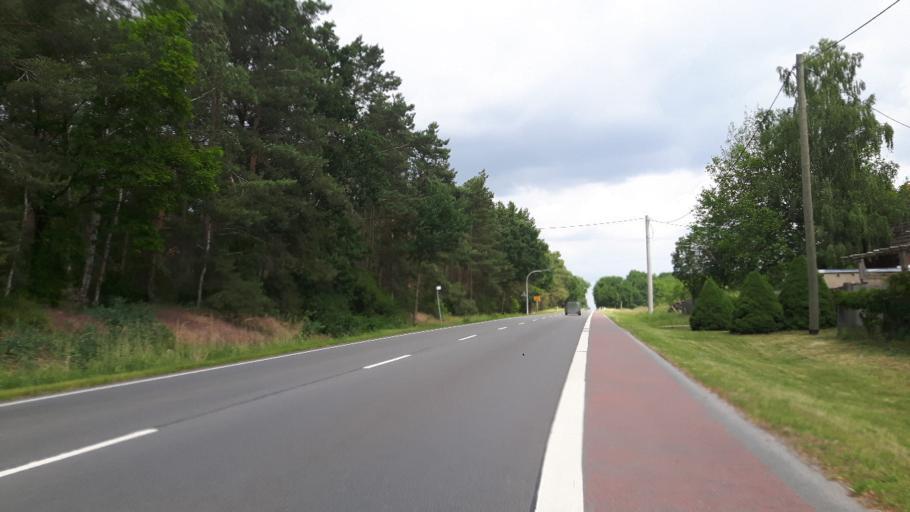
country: DE
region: Saxony-Anhalt
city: Schlaitz
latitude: 51.6728
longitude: 12.4444
